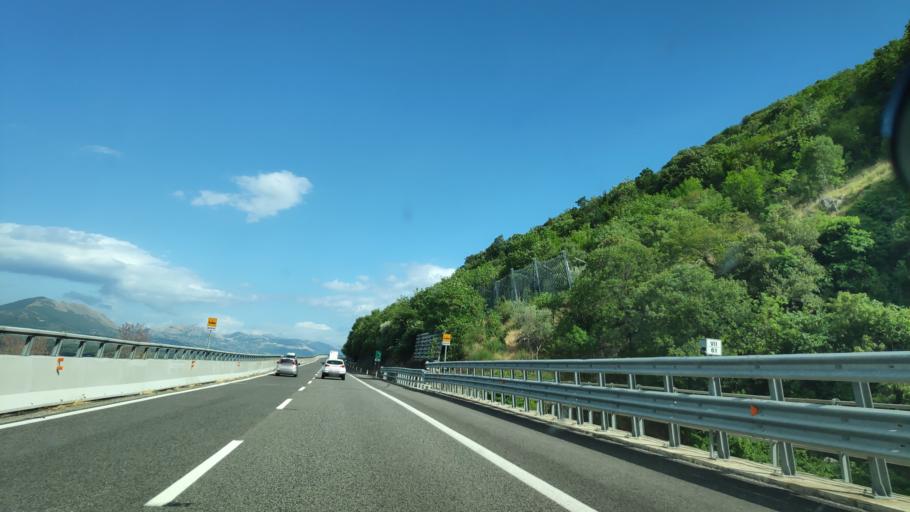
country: IT
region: Campania
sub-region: Provincia di Salerno
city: Sicignano degli Alburni
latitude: 40.5919
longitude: 15.3268
